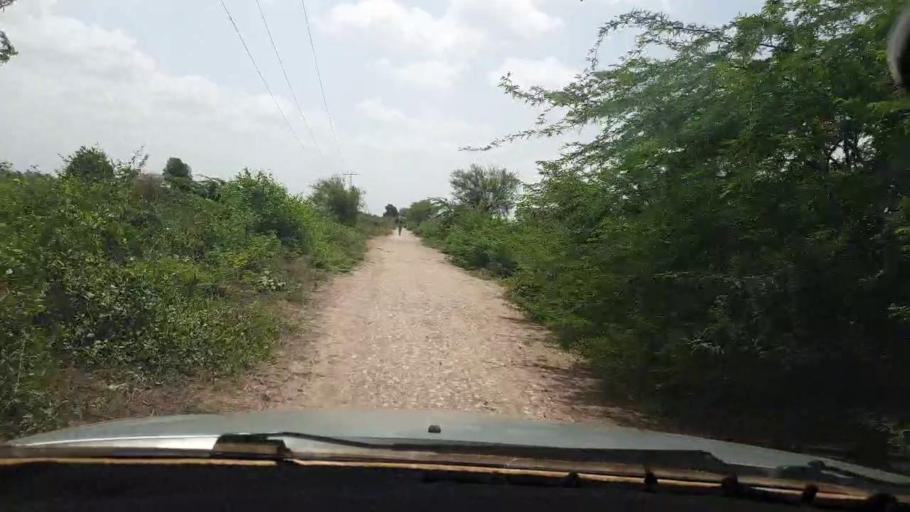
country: PK
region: Sindh
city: Tando Bago
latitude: 24.7552
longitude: 69.1702
